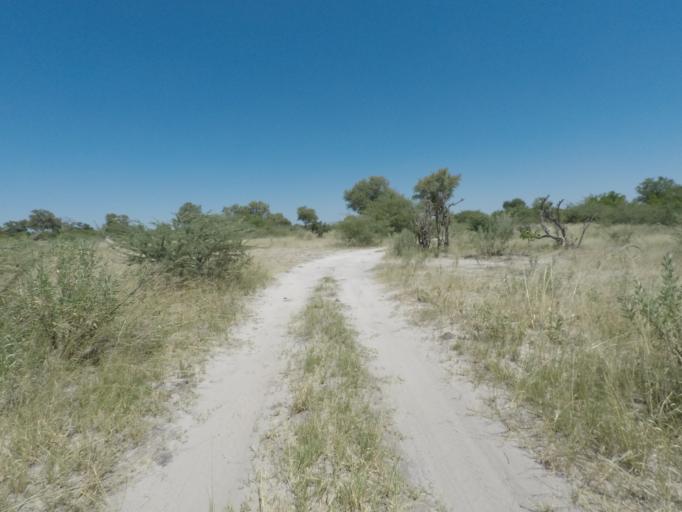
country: BW
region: North West
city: Maun
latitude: -19.4483
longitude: 23.5568
